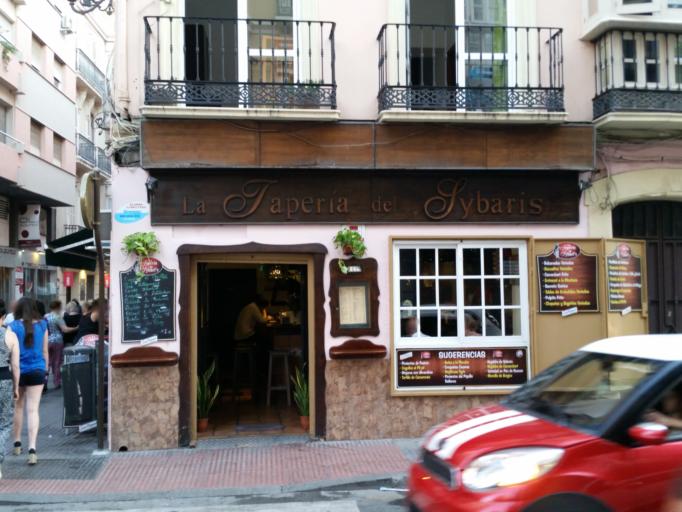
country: ES
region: Andalusia
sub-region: Provincia de Malaga
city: Malaga
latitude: 36.7238
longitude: -4.4198
